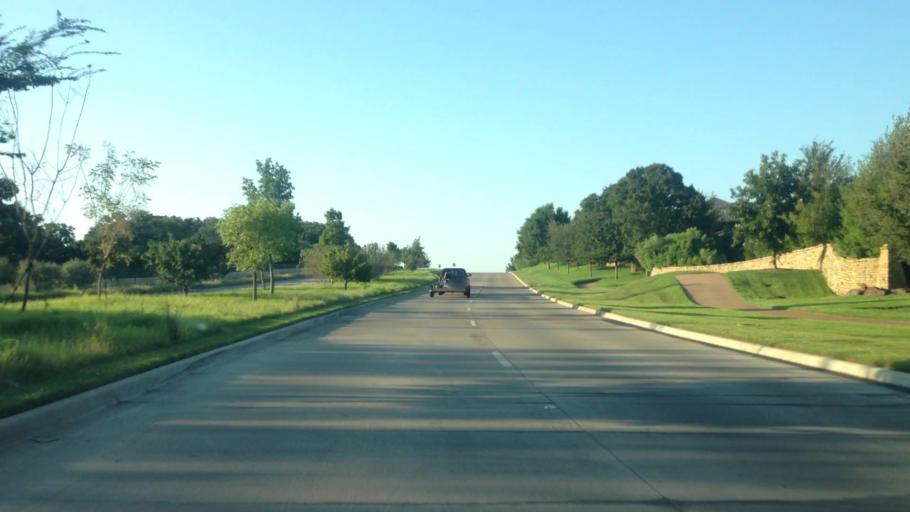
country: US
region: Texas
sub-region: Denton County
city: Trophy Club
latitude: 32.9699
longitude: -97.1860
